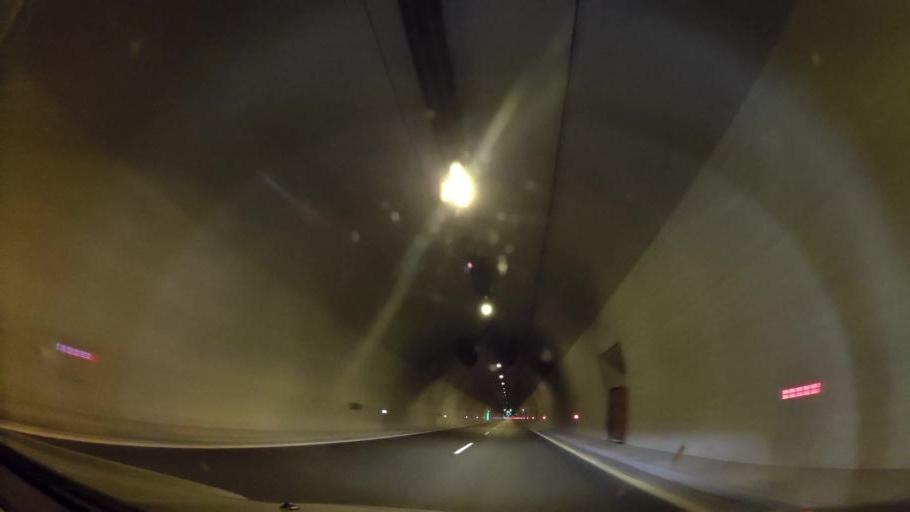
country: GR
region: Central Macedonia
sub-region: Nomos Imathias
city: Rizomata
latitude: 40.3837
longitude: 22.1272
